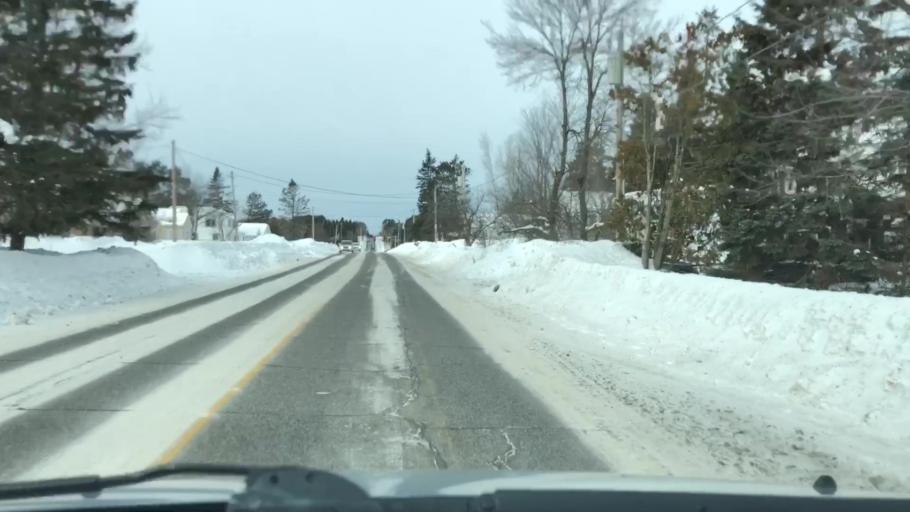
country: US
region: Minnesota
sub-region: Saint Louis County
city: Duluth
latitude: 46.7932
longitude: -92.1531
